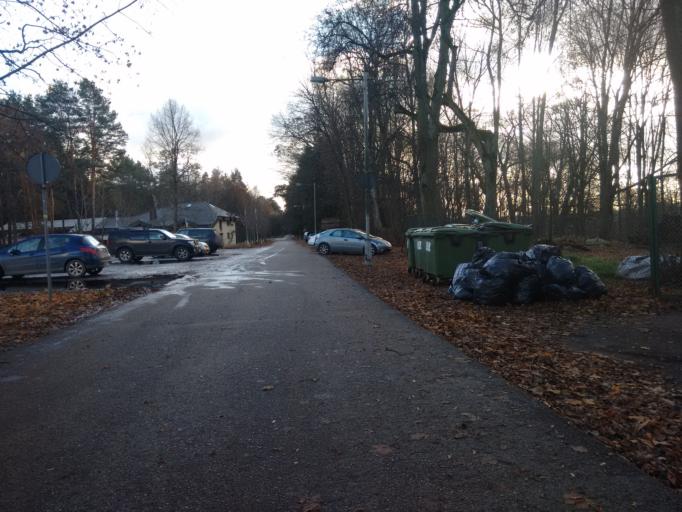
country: LT
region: Vilnius County
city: Vilkpede
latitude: 54.6835
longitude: 25.2341
